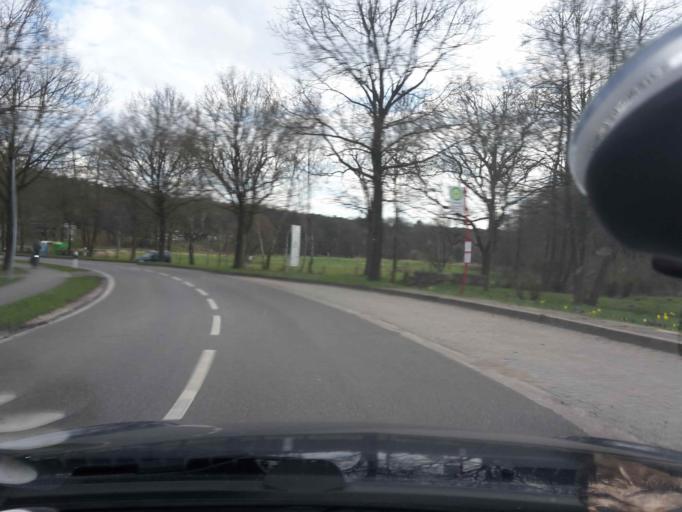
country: DE
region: Lower Saxony
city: Jesteburg
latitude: 53.2866
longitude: 9.9132
